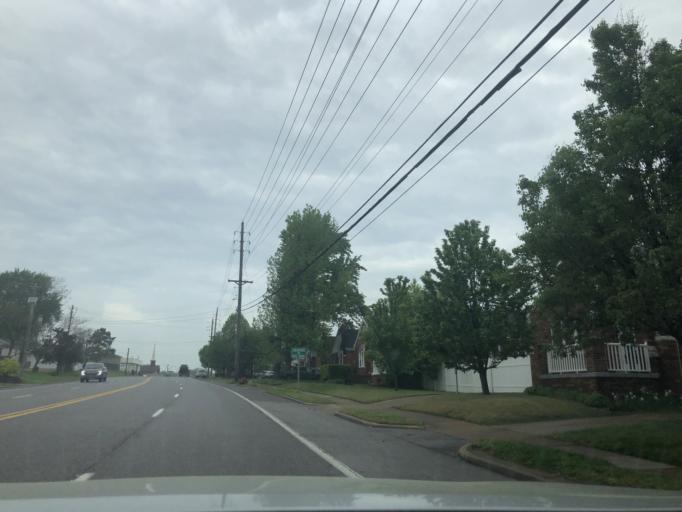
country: US
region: Missouri
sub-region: Saint Louis County
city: Affton
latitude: 38.5498
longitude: -90.3232
